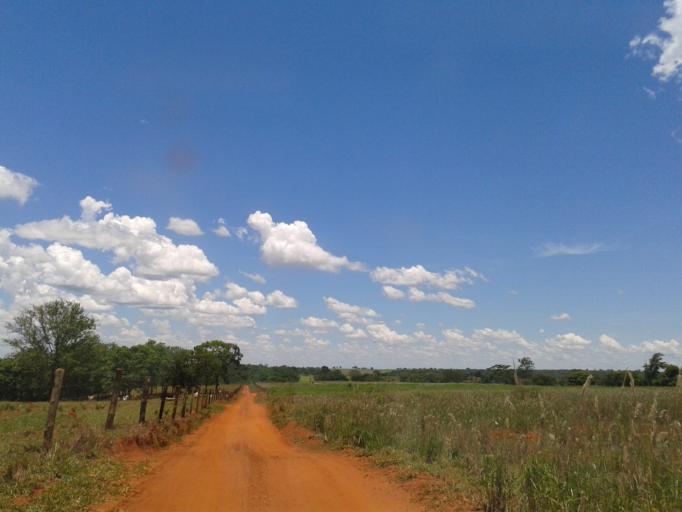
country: BR
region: Minas Gerais
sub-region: Centralina
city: Centralina
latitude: -18.7106
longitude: -49.1774
